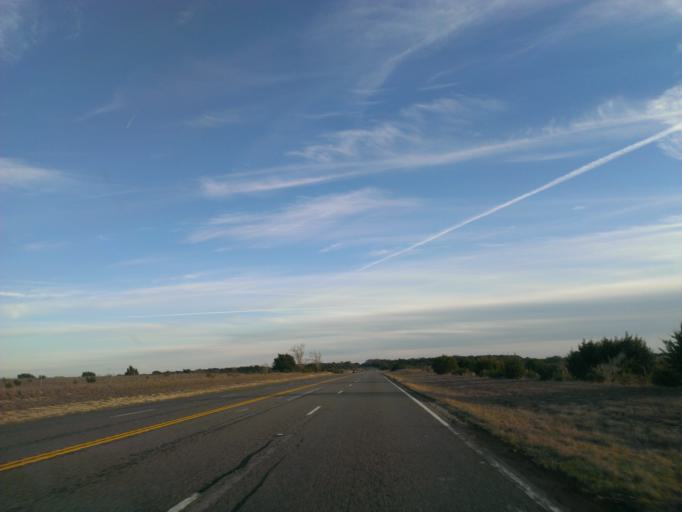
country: US
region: Texas
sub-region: Burnet County
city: Bertram
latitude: 30.9008
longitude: -97.9674
